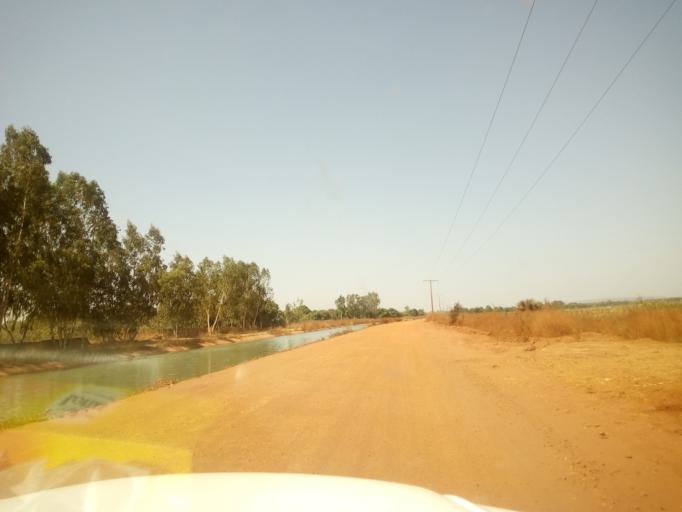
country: ML
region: Bamako
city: Bamako
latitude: 12.6216
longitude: -7.7623
